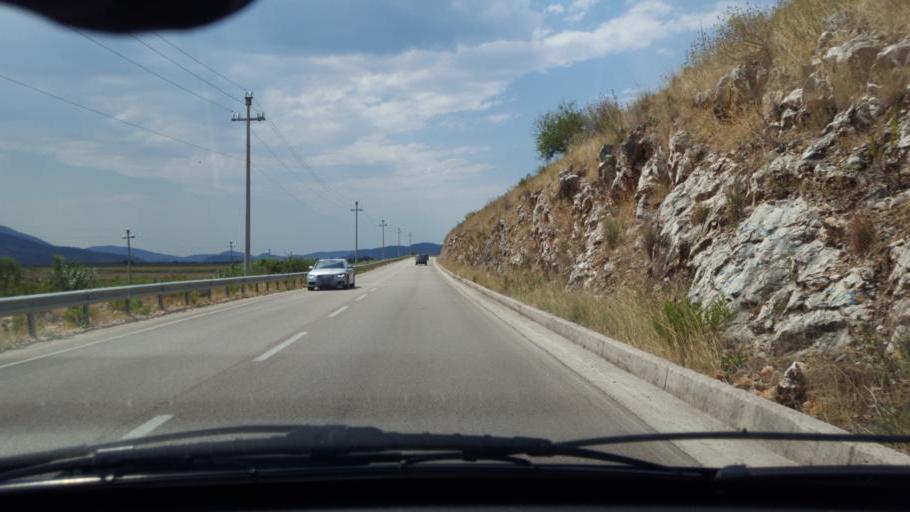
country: AL
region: Vlore
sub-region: Rrethi i Sarandes
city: Sarande
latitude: 39.8297
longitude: 20.0226
